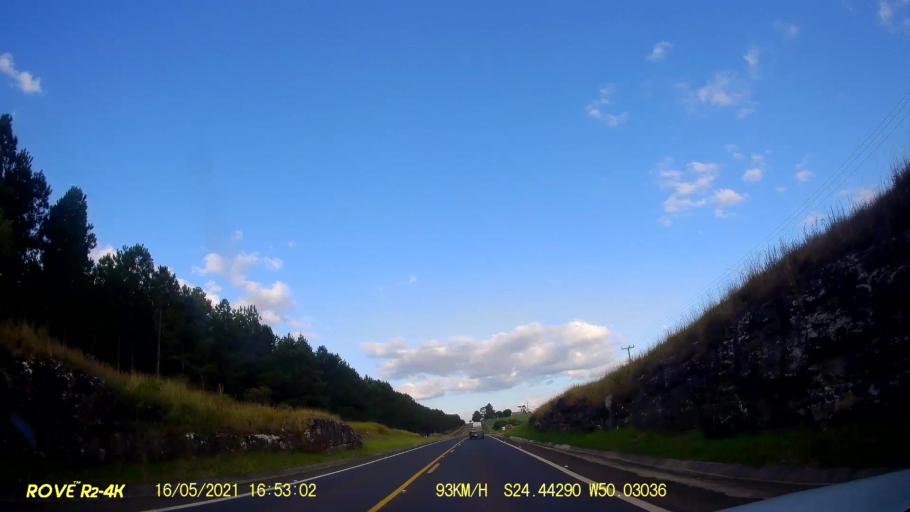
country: BR
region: Parana
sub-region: Pirai Do Sul
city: Pirai do Sul
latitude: -24.4426
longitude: -50.0309
